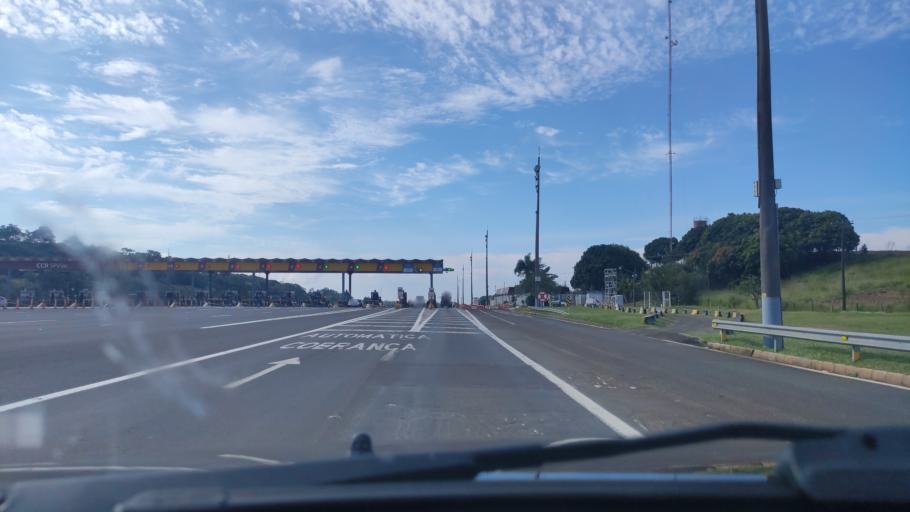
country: BR
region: Sao Paulo
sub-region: Itatinga
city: Itatinga
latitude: -23.0830
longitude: -48.5164
